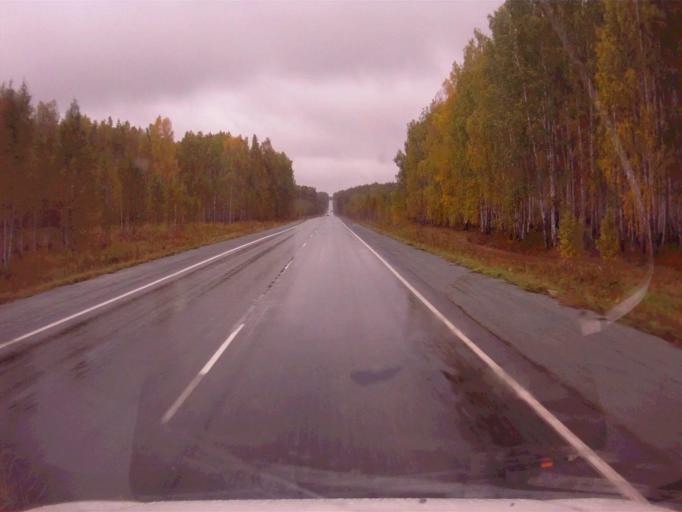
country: RU
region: Chelyabinsk
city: Tayginka
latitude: 55.5127
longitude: 60.6392
